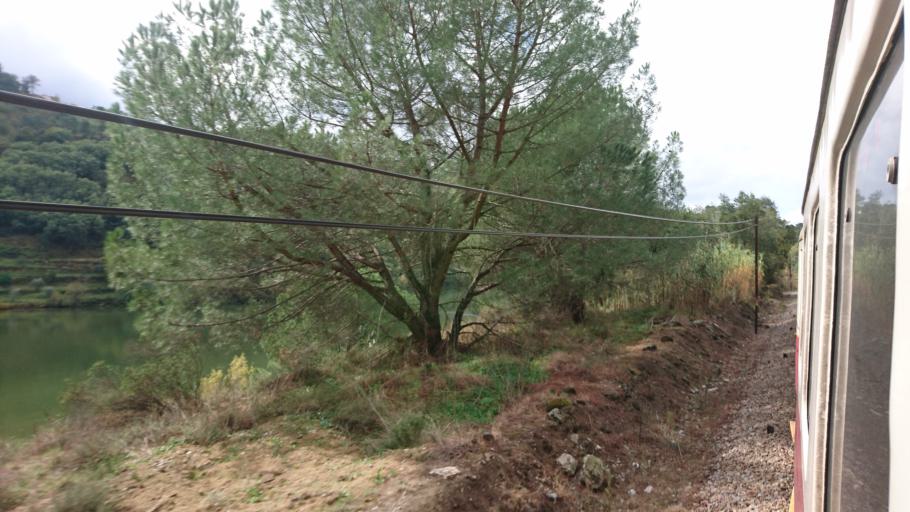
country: PT
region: Viseu
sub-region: Resende
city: Resende
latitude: 41.1214
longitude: -7.9171
